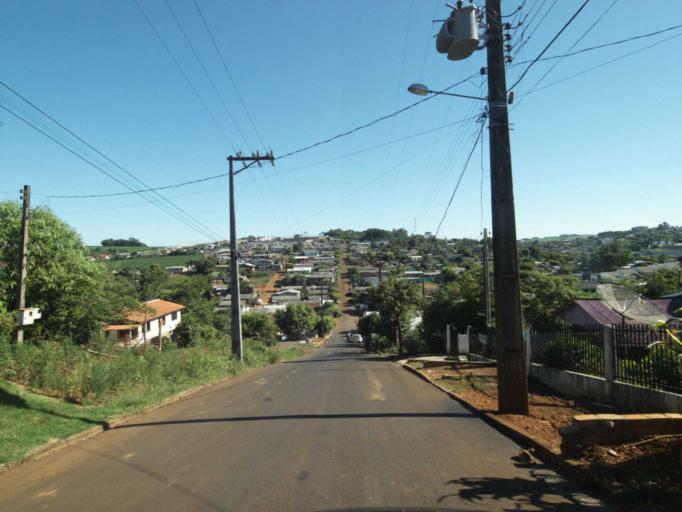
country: BR
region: Parana
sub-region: Coronel Vivida
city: Coronel Vivida
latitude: -25.9634
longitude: -52.8116
